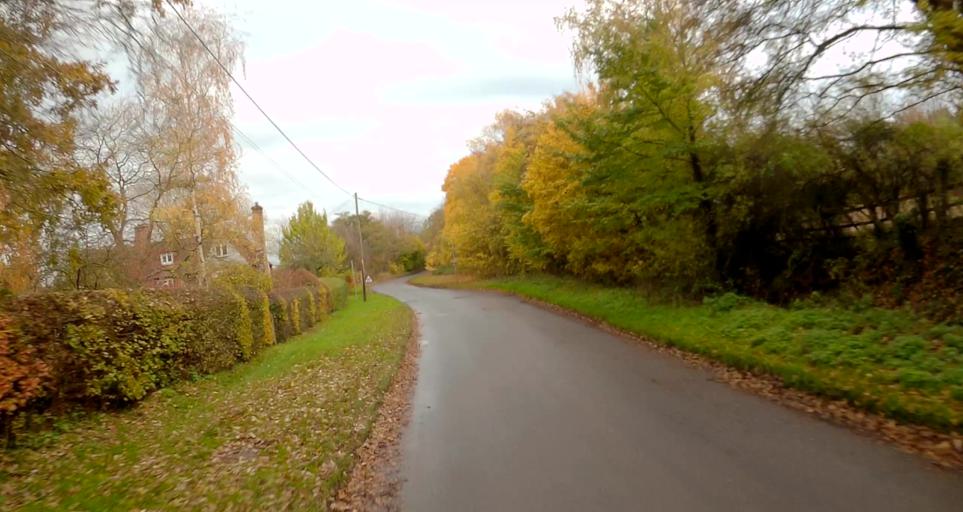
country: GB
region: England
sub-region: Hampshire
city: Long Sutton
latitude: 51.2197
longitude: -0.9389
